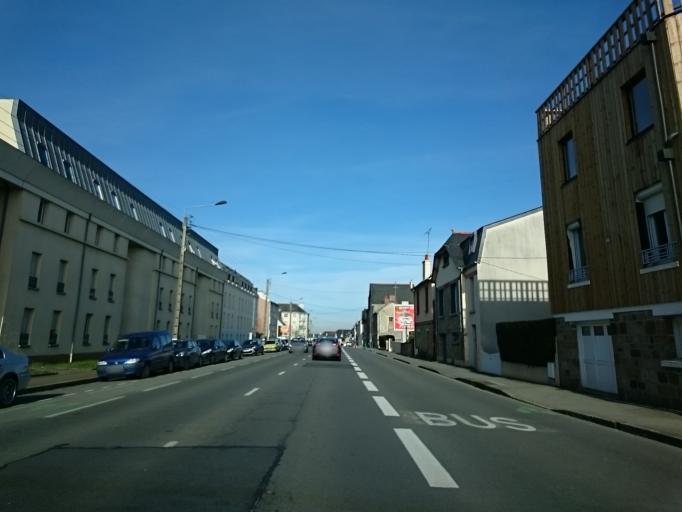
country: FR
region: Brittany
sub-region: Departement d'Ille-et-Vilaine
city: Rennes
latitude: 48.0941
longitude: -1.6490
